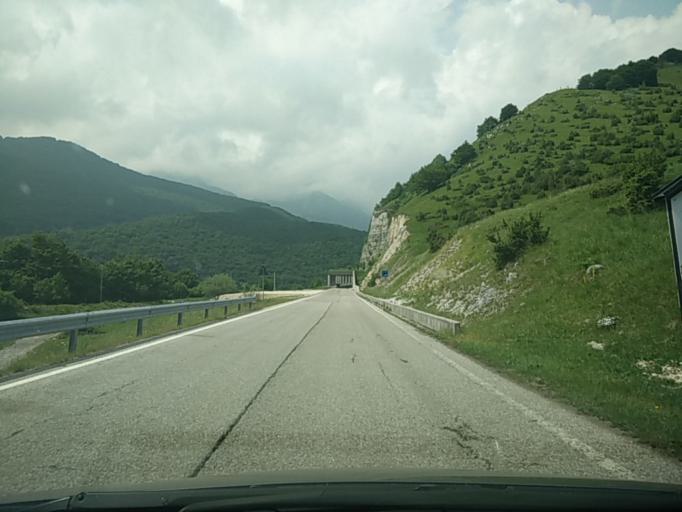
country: IT
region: Friuli Venezia Giulia
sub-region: Provincia di Pordenone
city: Budoia
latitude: 46.0888
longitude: 12.5290
